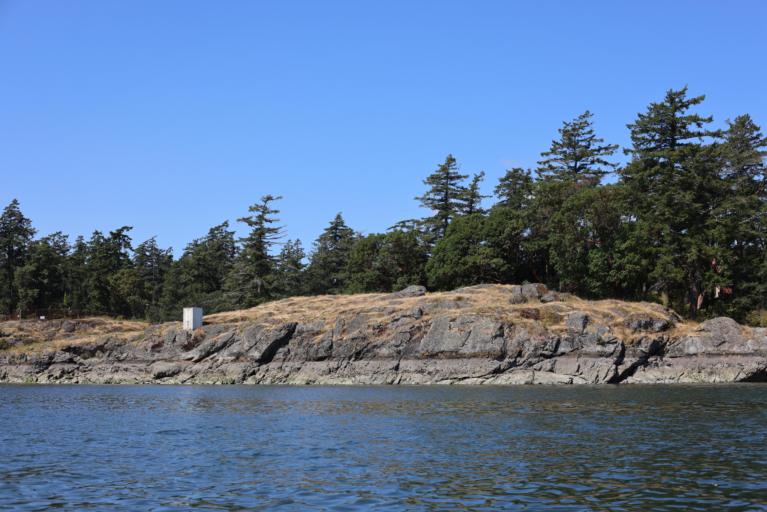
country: CA
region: British Columbia
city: Colwood
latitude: 48.4480
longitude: -123.4472
